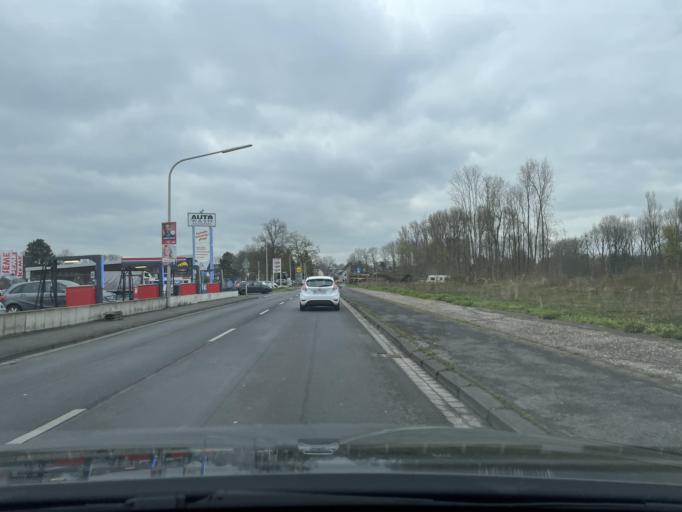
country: DE
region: North Rhine-Westphalia
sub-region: Regierungsbezirk Dusseldorf
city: Monchengladbach
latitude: 51.1635
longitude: 6.4603
